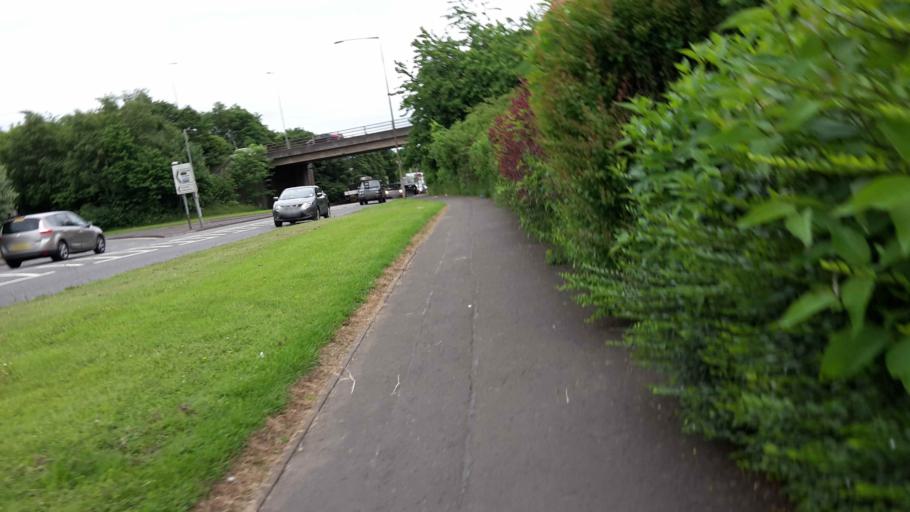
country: GB
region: Scotland
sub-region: South Lanarkshire
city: Bothwell
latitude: 55.7910
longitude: -4.0819
